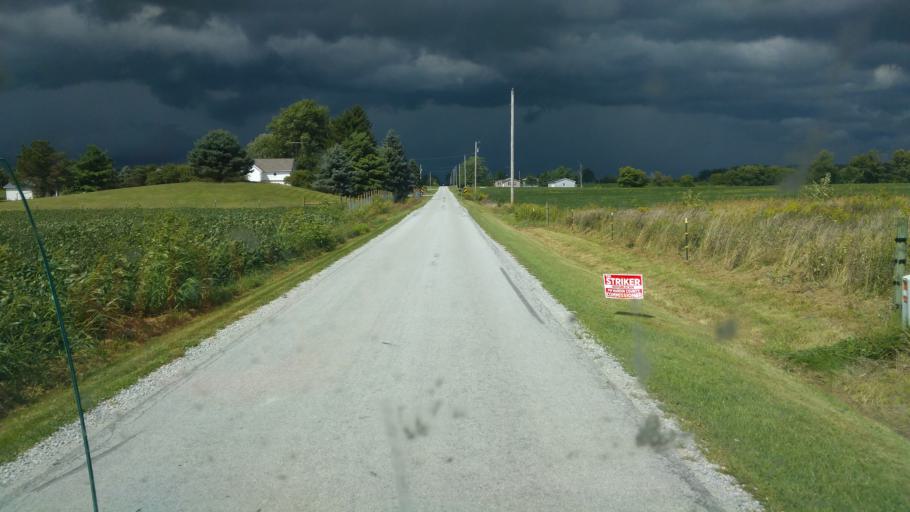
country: US
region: Ohio
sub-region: Hardin County
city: Kenton
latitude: 40.6366
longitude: -83.5154
